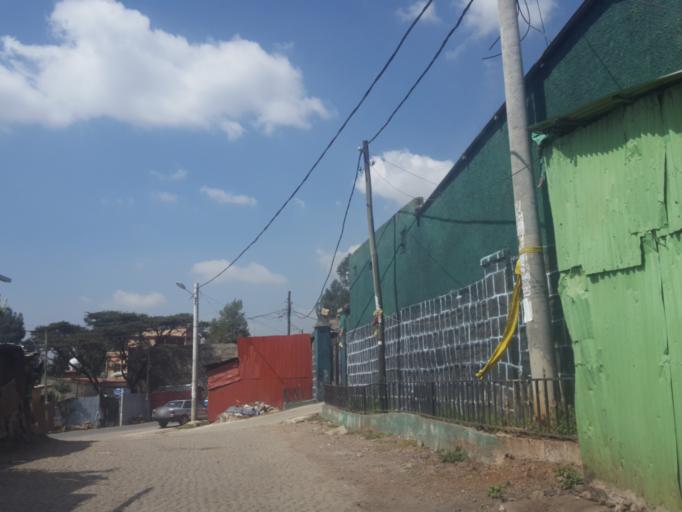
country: ET
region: Adis Abeba
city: Addis Ababa
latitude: 9.0566
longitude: 38.7276
